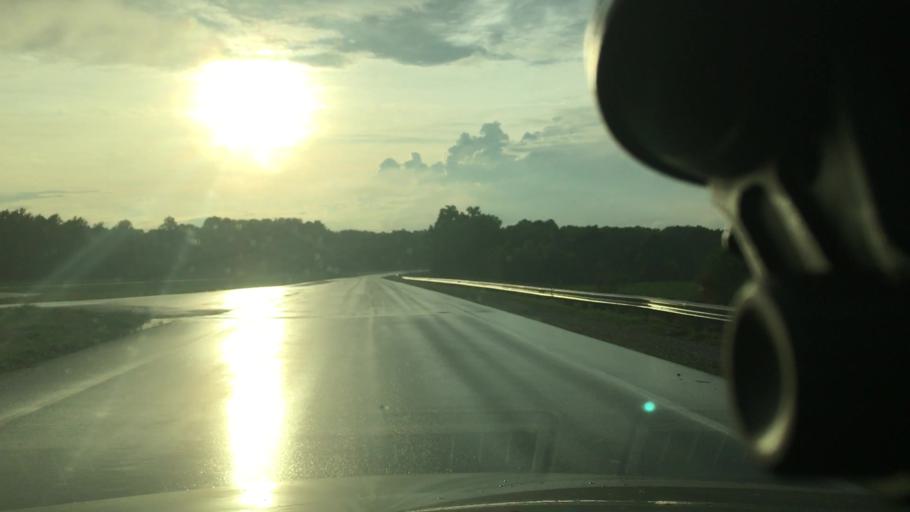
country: US
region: North Carolina
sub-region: Wilson County
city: Wilson
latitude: 35.7638
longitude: -78.0274
